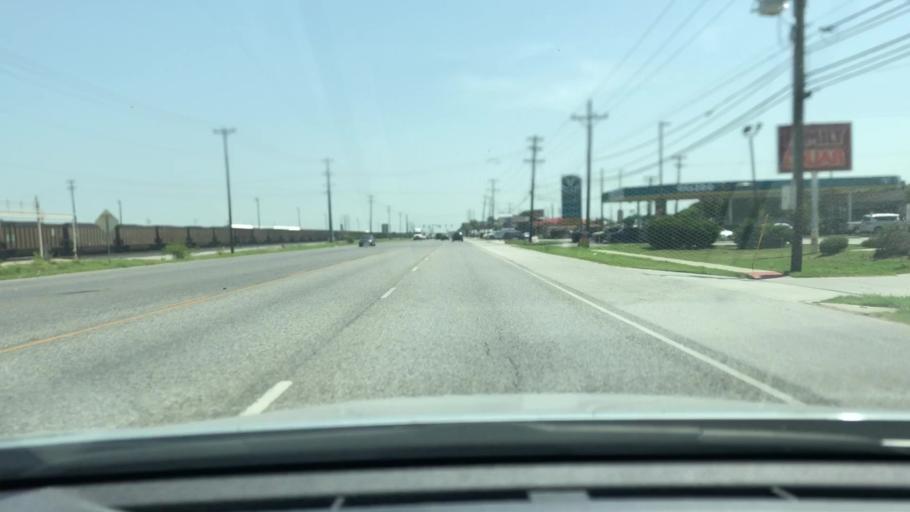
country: US
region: Texas
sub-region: Bexar County
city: Kirby
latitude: 29.4616
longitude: -98.4010
